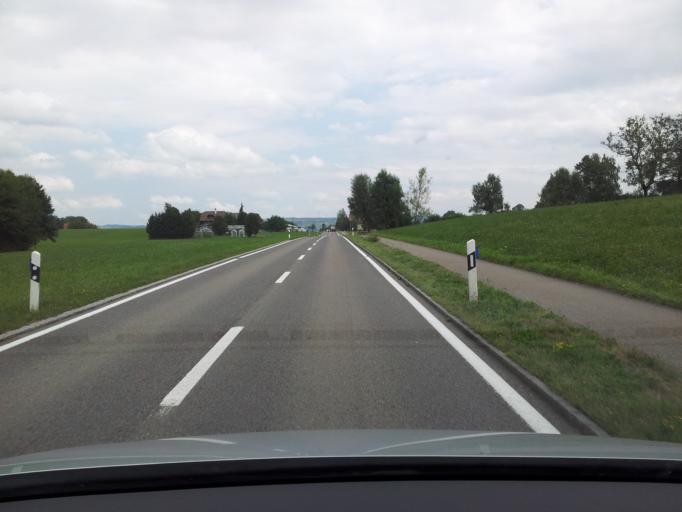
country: CH
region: Lucerne
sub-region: Sursee District
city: Buttisholz
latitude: 47.1247
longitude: 8.1100
